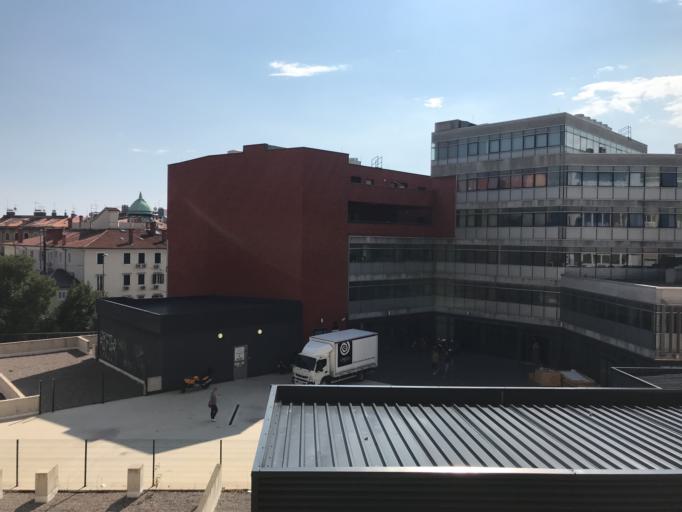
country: HR
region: Primorsko-Goranska
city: Drenova
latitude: 45.3301
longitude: 14.4397
